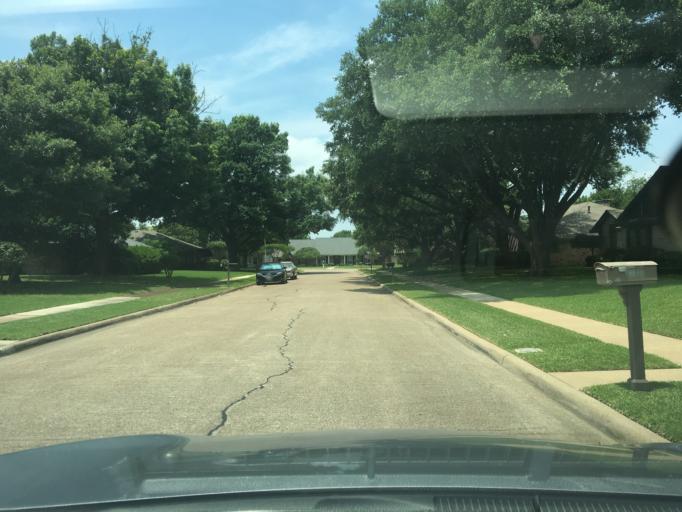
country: US
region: Texas
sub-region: Dallas County
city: Richardson
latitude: 32.9592
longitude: -96.6918
